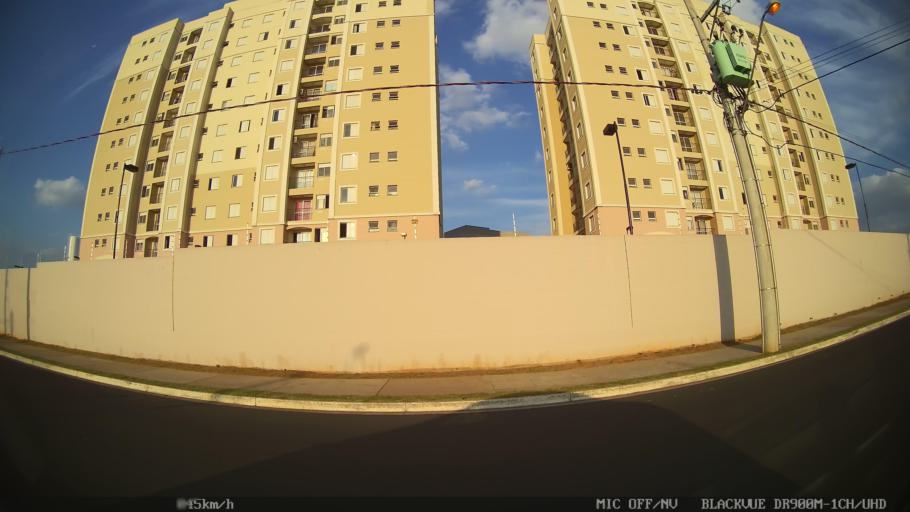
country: BR
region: Sao Paulo
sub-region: Hortolandia
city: Hortolandia
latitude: -22.8946
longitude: -47.1624
